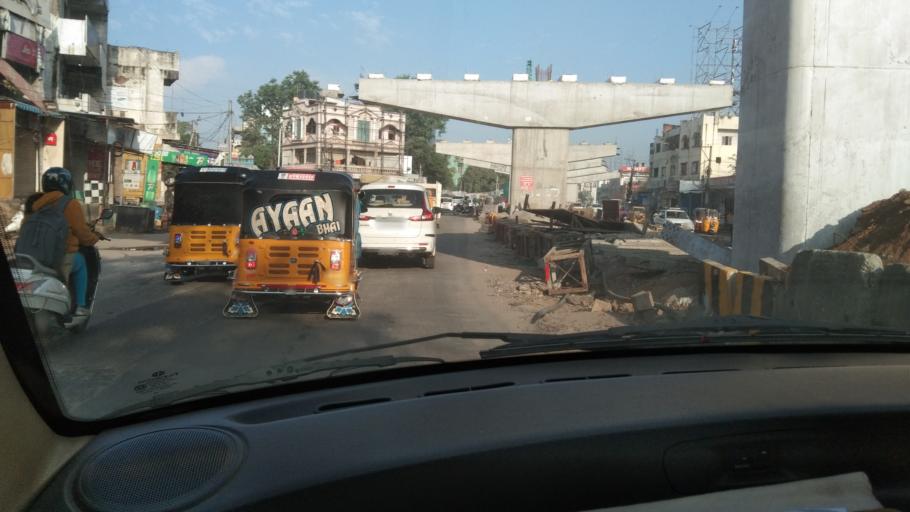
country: IN
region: Telangana
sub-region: Hyderabad
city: Hyderabad
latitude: 17.4123
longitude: 78.3955
